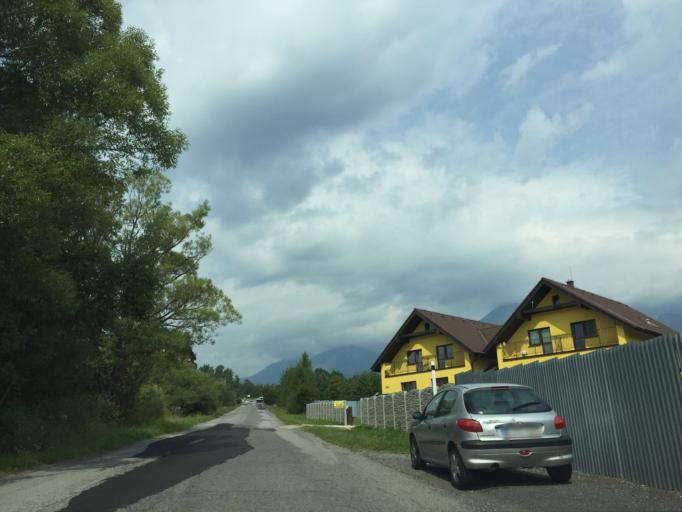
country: SK
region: Presovsky
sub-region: Okres Poprad
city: Nova Lesna
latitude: 49.1228
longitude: 20.2624
